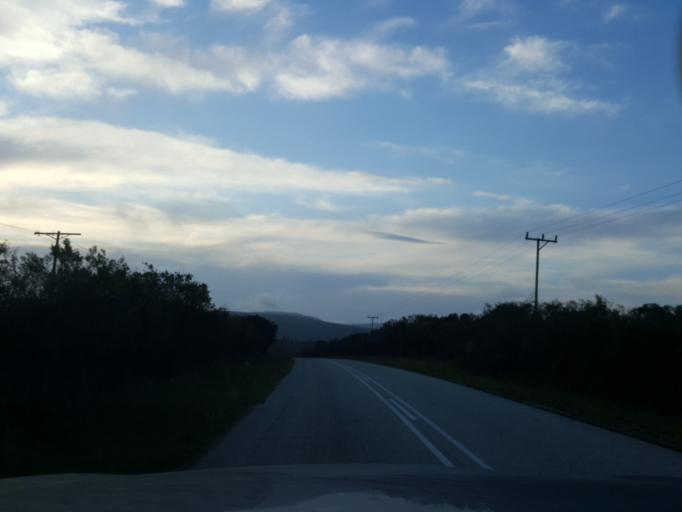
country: ZA
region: Eastern Cape
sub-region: Cacadu District Municipality
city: Grahamstown
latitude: -33.3911
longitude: 26.4748
